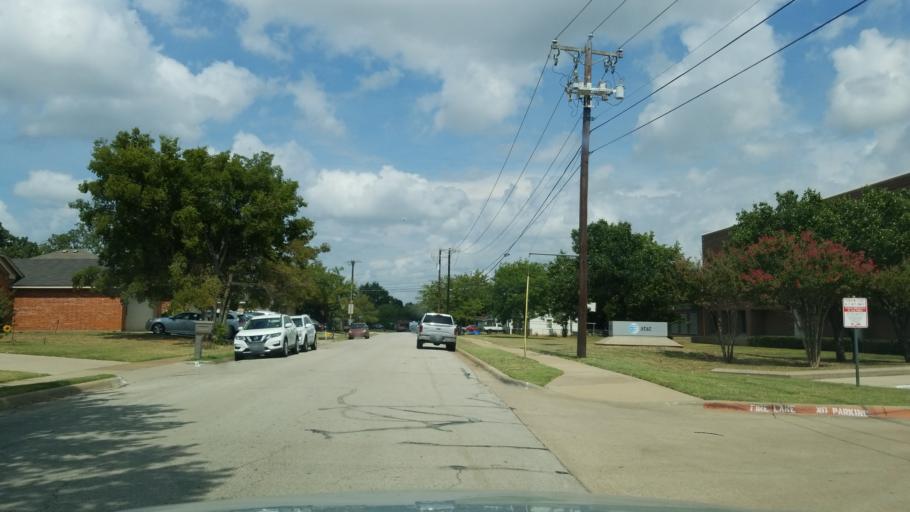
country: US
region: Texas
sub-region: Tarrant County
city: Euless
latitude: 32.8408
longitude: -97.0862
